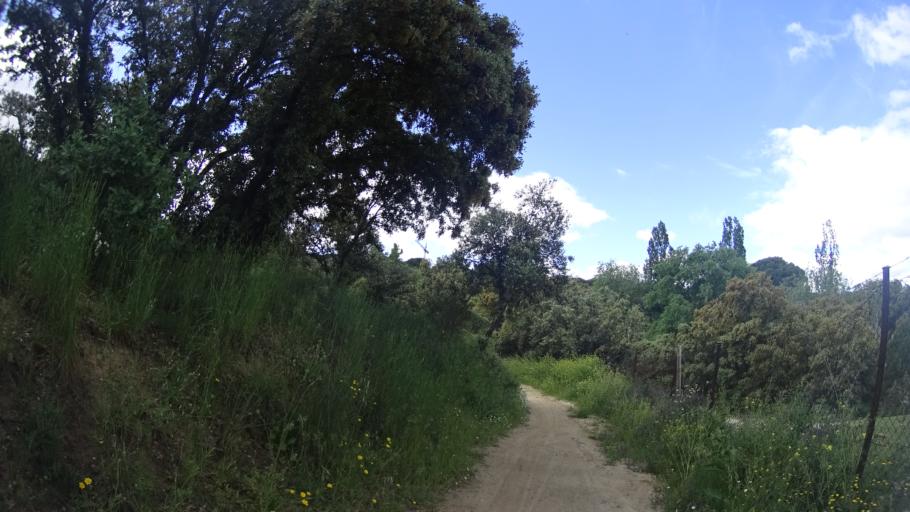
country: ES
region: Madrid
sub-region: Provincia de Madrid
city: Villaviciosa de Odon
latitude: 40.3889
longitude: -3.9402
